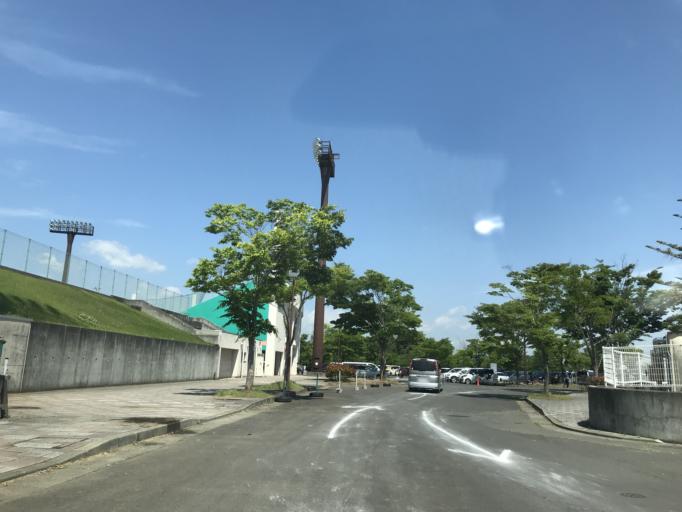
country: JP
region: Iwate
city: Ichinoseki
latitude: 38.9180
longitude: 141.1243
